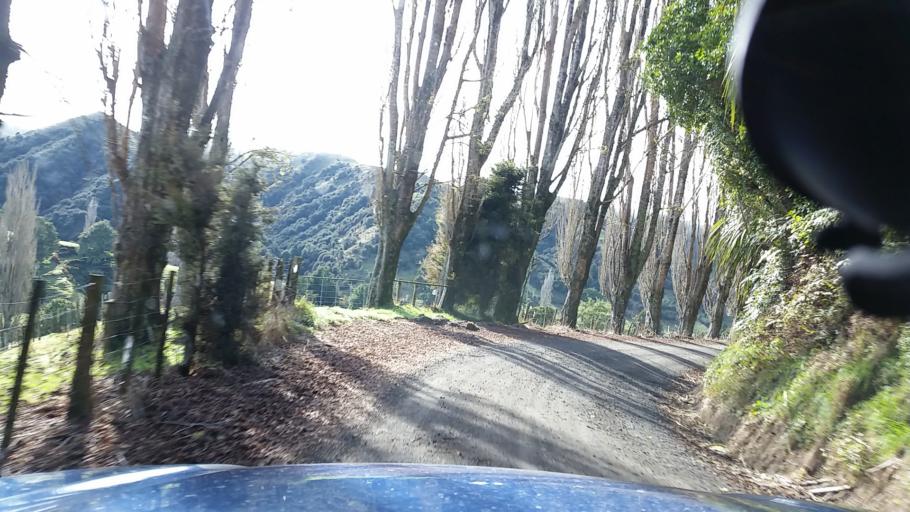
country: NZ
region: Taranaki
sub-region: New Plymouth District
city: Waitara
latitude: -39.0322
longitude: 174.7893
